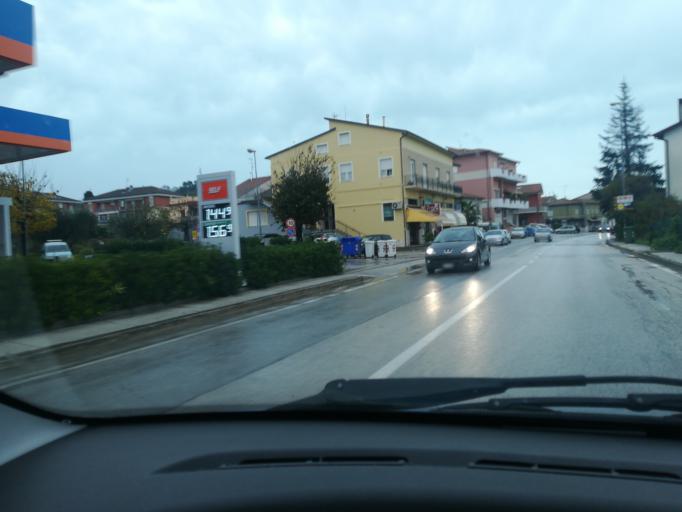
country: IT
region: The Marches
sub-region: Provincia di Macerata
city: Santa Maria Apparente
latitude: 43.2968
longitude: 13.6899
